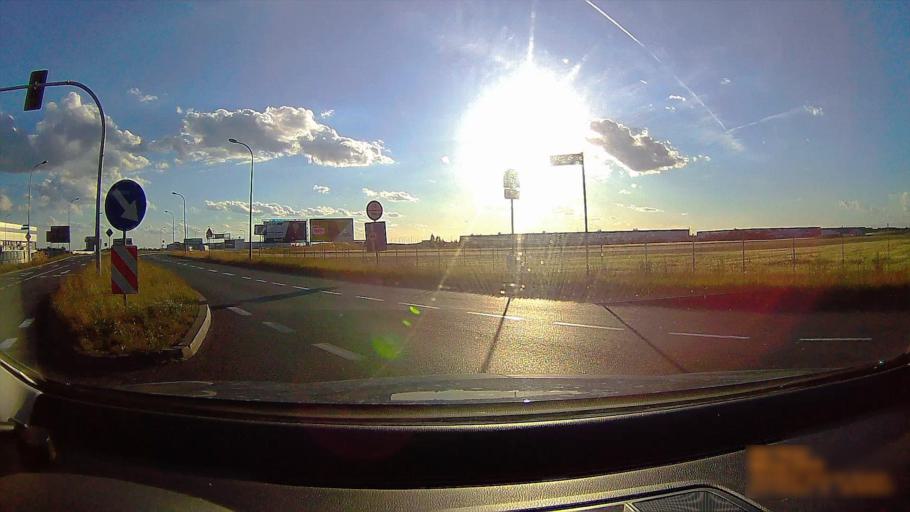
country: PL
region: Greater Poland Voivodeship
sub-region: Kalisz
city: Kalisz
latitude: 51.7398
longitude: 18.0435
